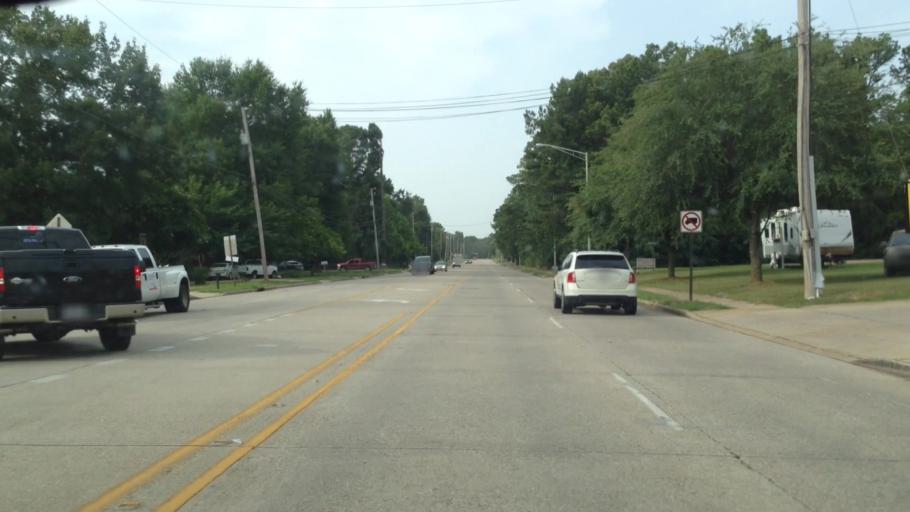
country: US
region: Louisiana
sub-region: De Soto Parish
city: Stonewall
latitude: 32.4017
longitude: -93.8147
